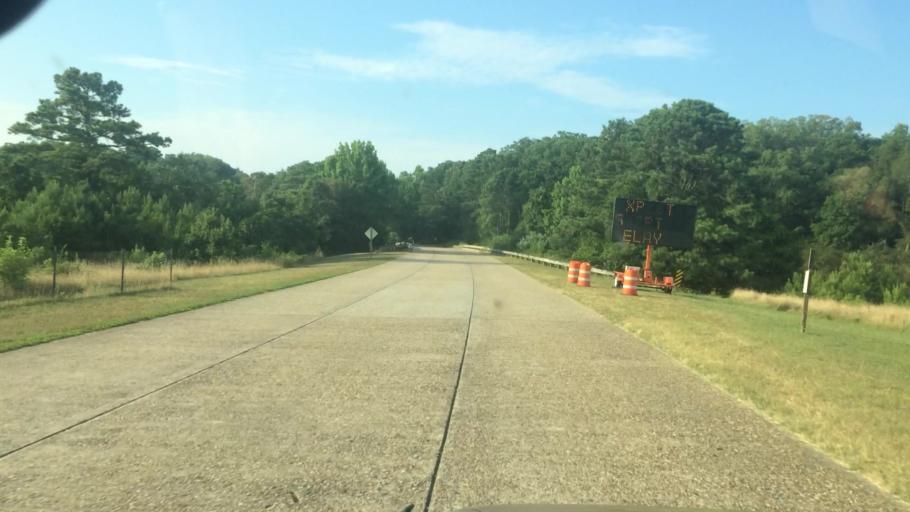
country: US
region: Virginia
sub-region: City of Williamsburg
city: Williamsburg
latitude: 37.2250
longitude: -76.6951
